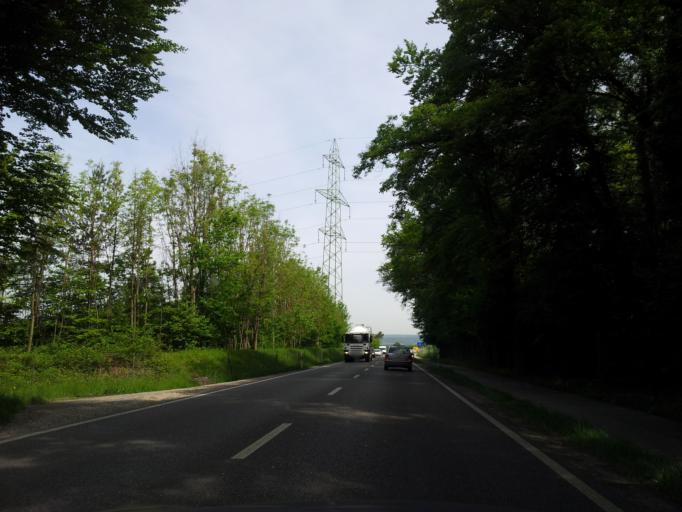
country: CH
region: Zurich
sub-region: Bezirk Buelach
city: Buelach / Soligaenter
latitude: 47.5484
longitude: 8.5299
